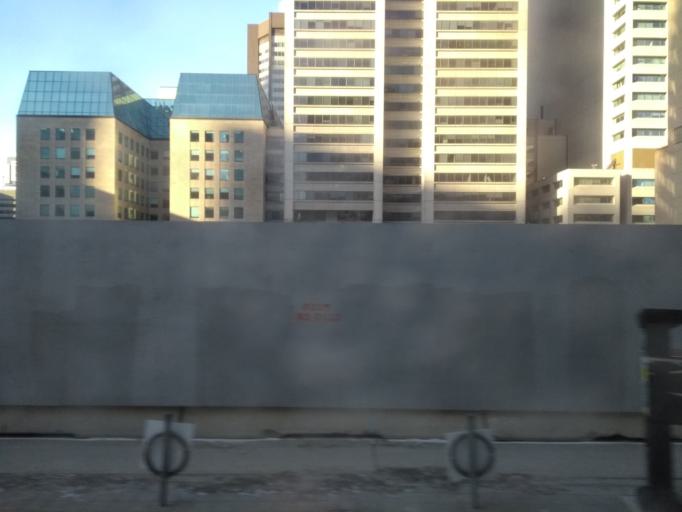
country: CA
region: Ontario
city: Toronto
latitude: 43.6543
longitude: -79.3858
